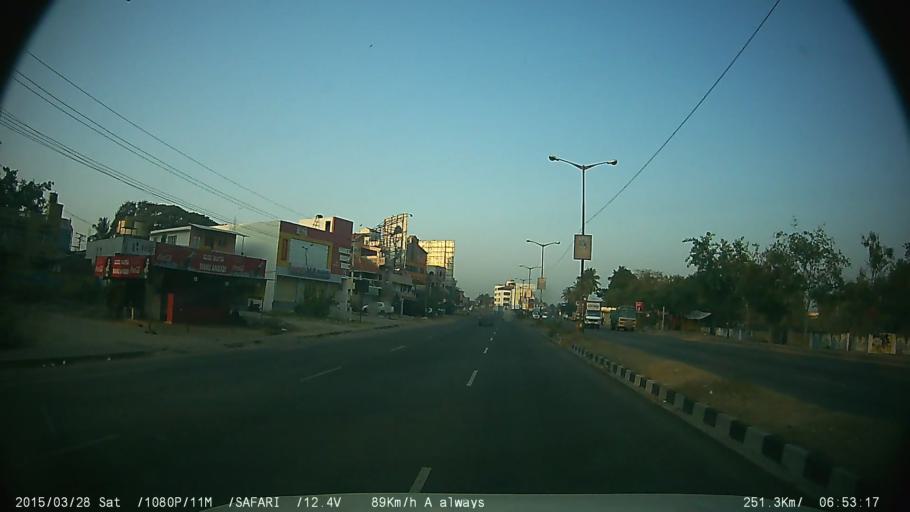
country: IN
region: Karnataka
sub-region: Mandya
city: Maddur
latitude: 12.5844
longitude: 77.0393
